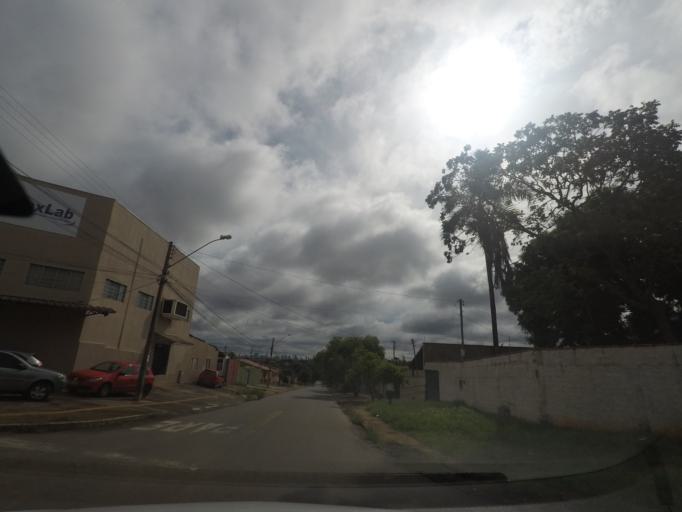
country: BR
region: Goias
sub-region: Goiania
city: Goiania
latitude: -16.7415
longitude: -49.3251
